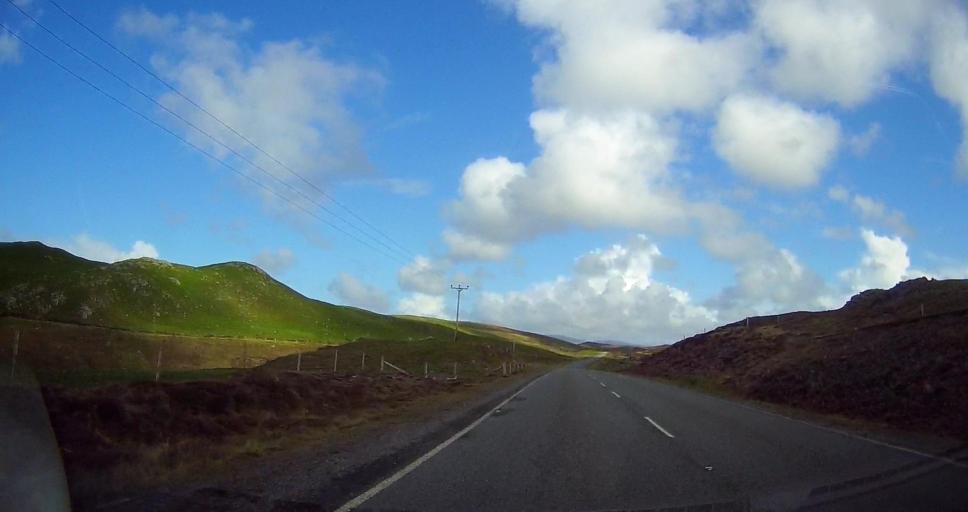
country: GB
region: Scotland
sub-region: Shetland Islands
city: Lerwick
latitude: 60.4231
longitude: -1.3951
